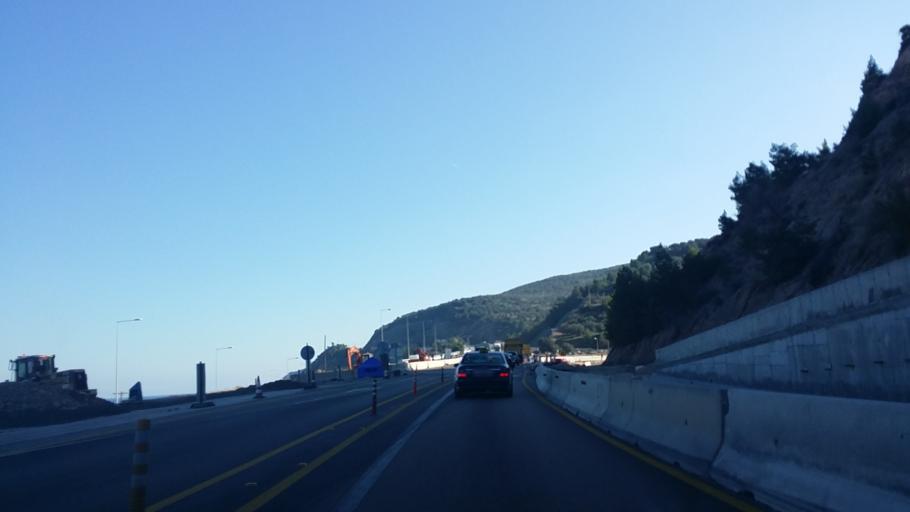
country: GR
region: West Greece
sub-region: Nomos Achaias
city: Akrata
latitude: 38.1767
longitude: 22.2364
